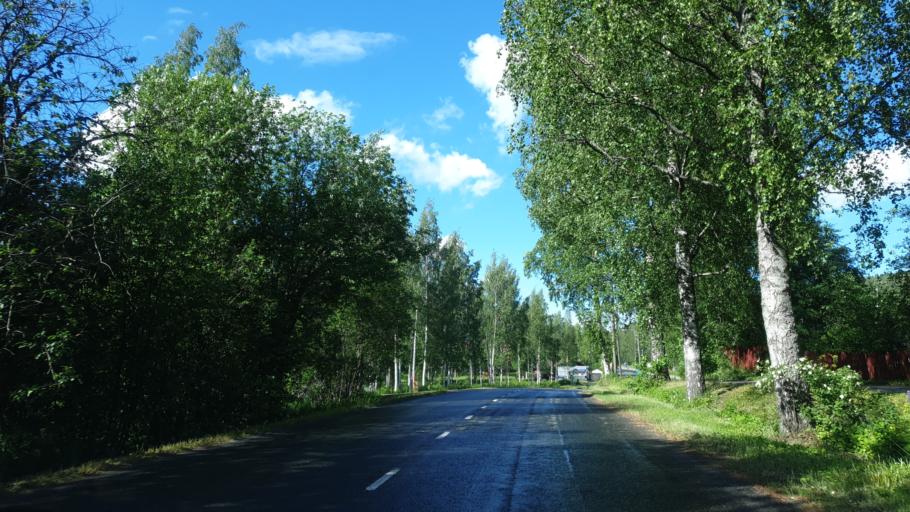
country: FI
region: Northern Savo
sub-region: Kuopio
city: Kuopio
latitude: 62.9208
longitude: 27.6305
